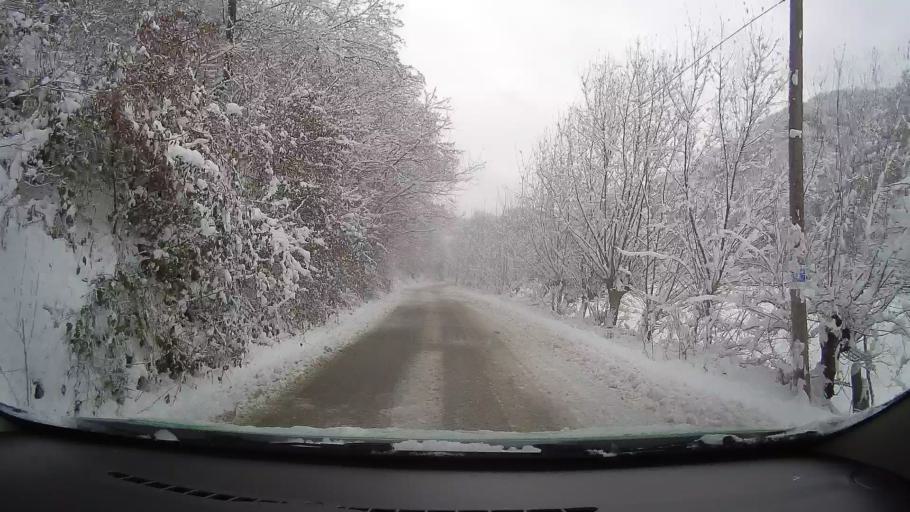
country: RO
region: Alba
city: Pianu de Sus
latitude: 45.8634
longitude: 23.4982
